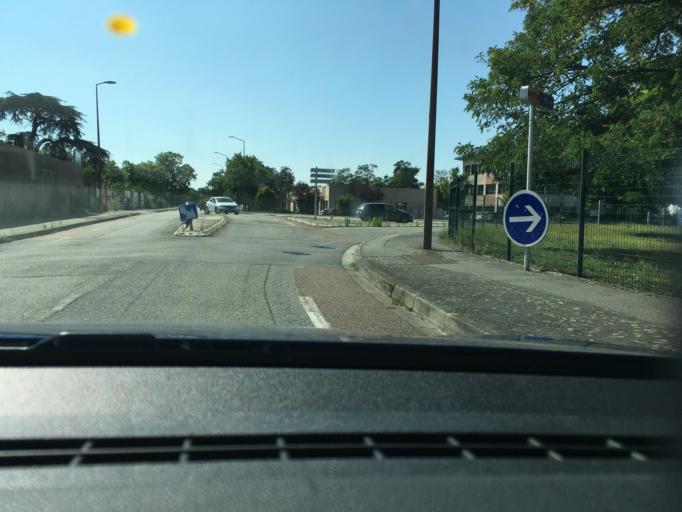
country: FR
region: Midi-Pyrenees
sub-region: Departement de la Haute-Garonne
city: Portet-sur-Garonne
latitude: 43.5668
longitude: 1.3853
